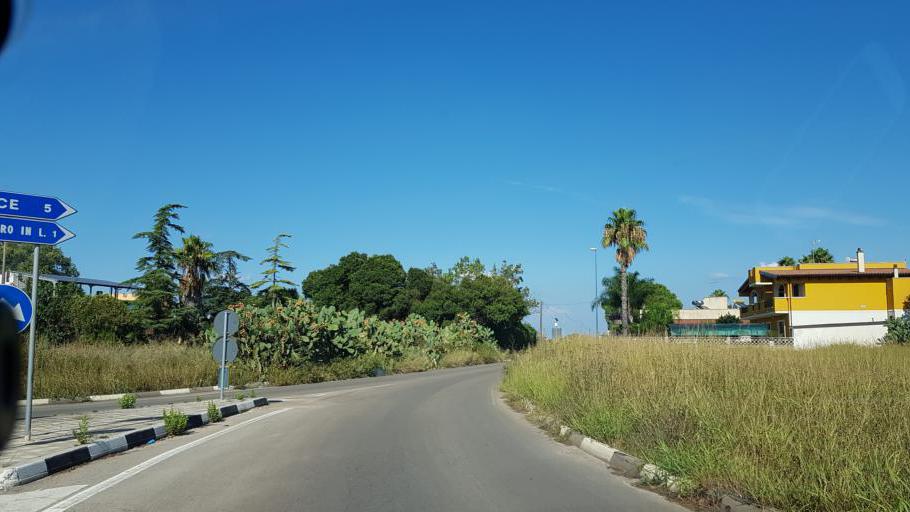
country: IT
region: Apulia
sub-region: Provincia di Lecce
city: San Pietro in Lama
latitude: 40.3015
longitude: 18.1158
